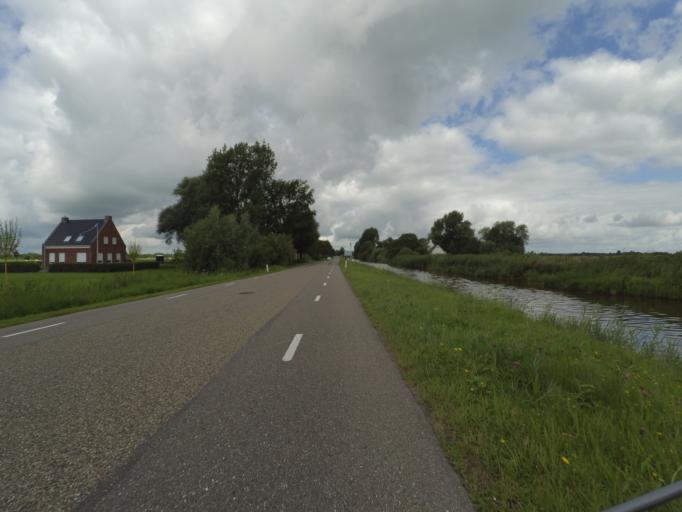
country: NL
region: Friesland
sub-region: Gemeente Kollumerland en Nieuwkruisland
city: Kollum
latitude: 53.2640
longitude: 6.1666
